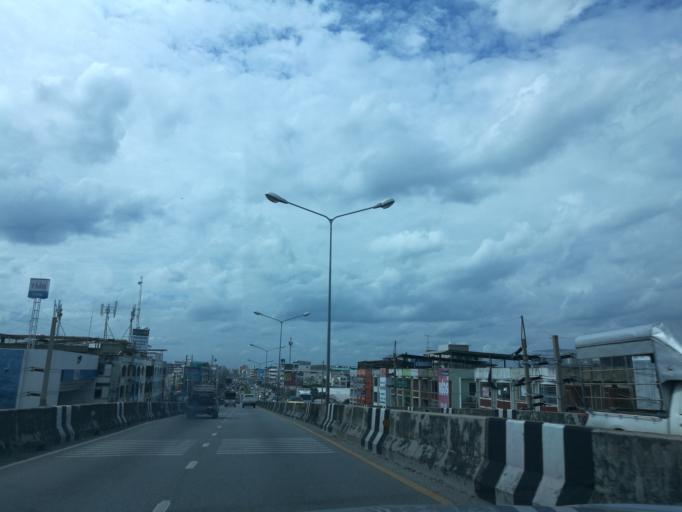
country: TH
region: Bangkok
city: Bang Khun Thian
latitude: 13.6572
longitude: 100.4300
